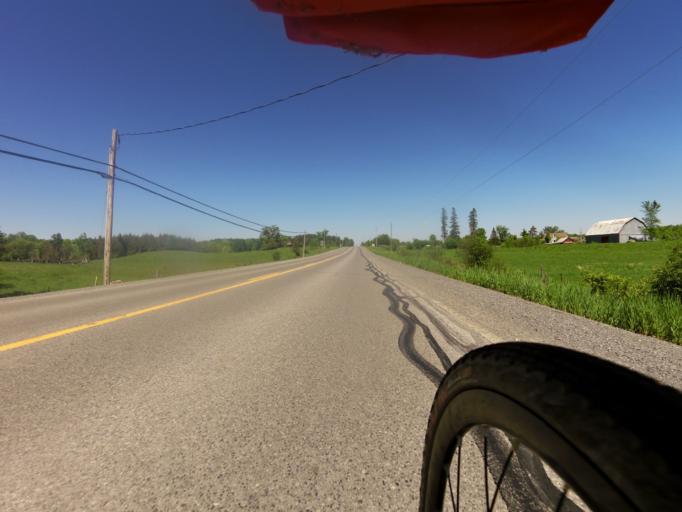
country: CA
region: Ontario
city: Carleton Place
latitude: 45.1628
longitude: -76.2905
